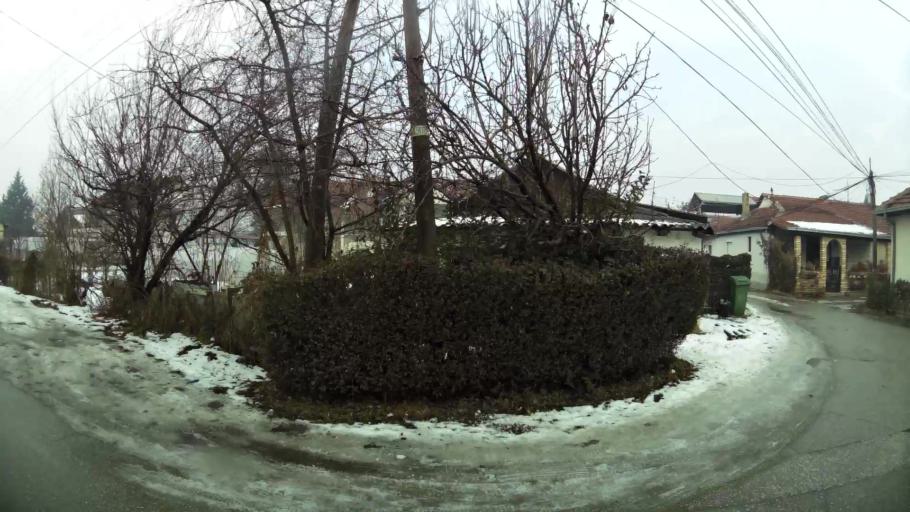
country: MK
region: Ilinden
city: Jurumleri
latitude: 41.9736
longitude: 21.5418
